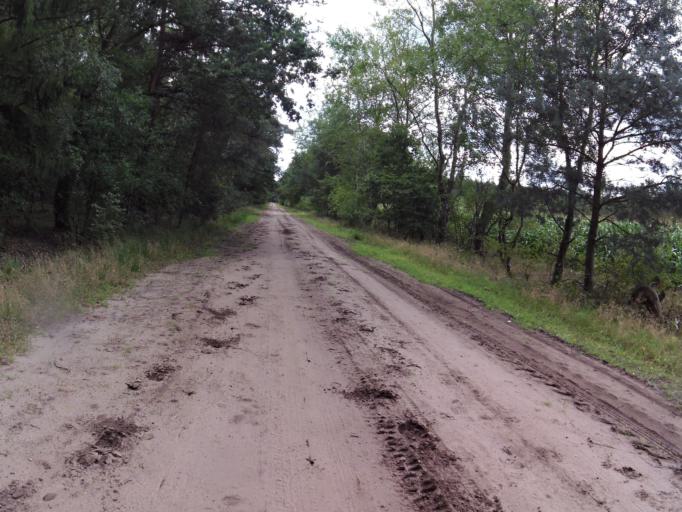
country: DE
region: Lower Saxony
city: Sandbostel
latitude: 53.3723
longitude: 9.1514
